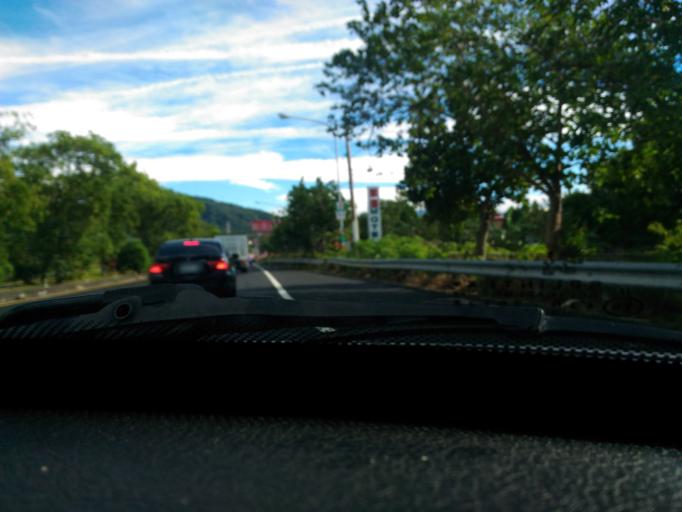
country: TW
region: Taiwan
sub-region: Hsinchu
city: Zhubei
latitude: 24.7651
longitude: 121.0834
